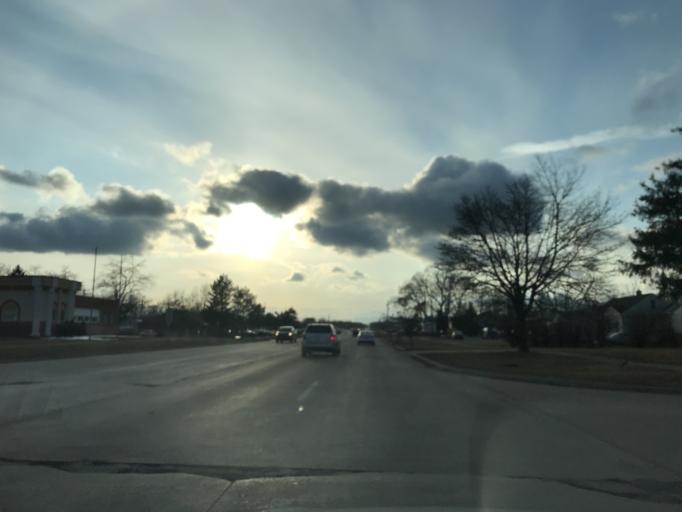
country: US
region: Michigan
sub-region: Wayne County
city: Redford
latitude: 42.4274
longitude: -83.3294
